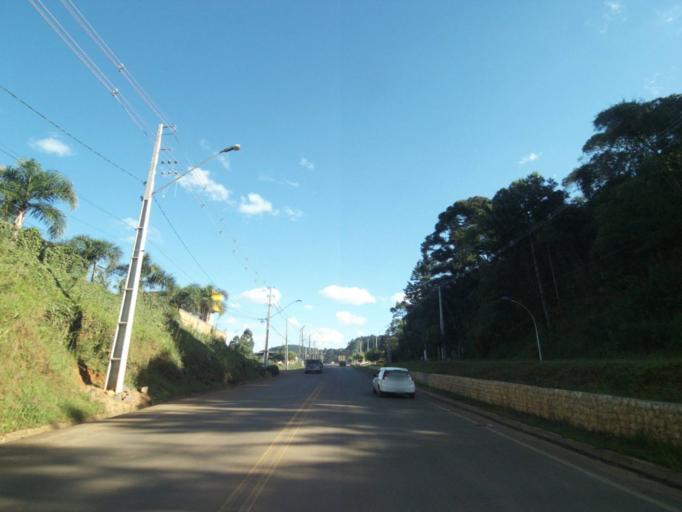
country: BR
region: Parana
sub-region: Uniao Da Vitoria
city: Uniao da Vitoria
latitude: -26.1545
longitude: -51.5427
